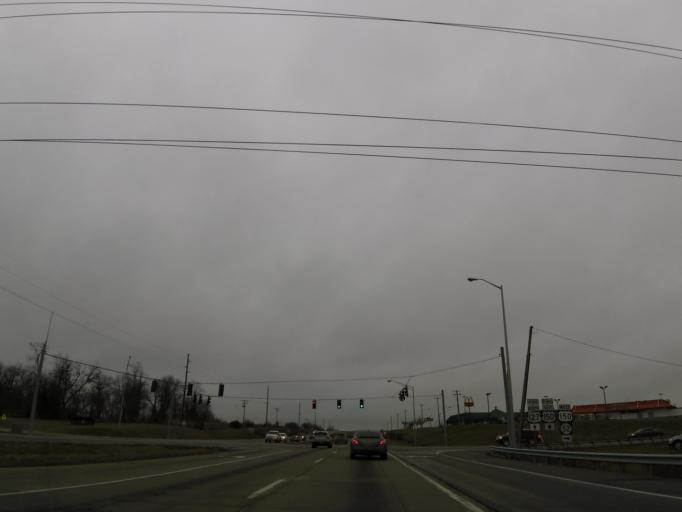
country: US
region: Kentucky
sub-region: Boyle County
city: Danville
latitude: 37.6492
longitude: -84.8033
